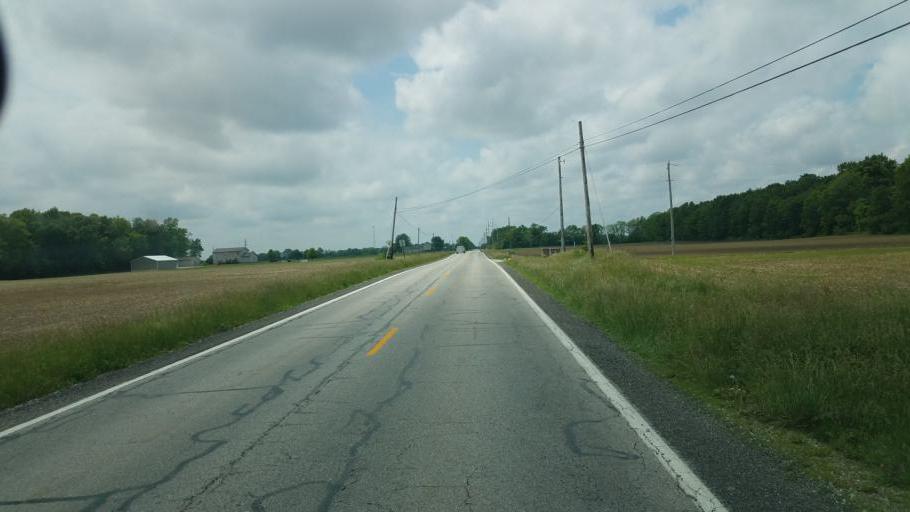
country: US
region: Ohio
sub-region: Marion County
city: Prospect
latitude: 40.4500
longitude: -83.2005
